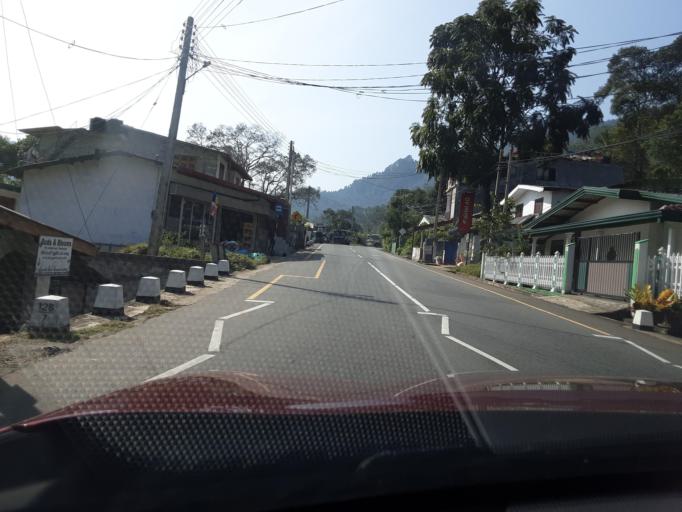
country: LK
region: Uva
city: Badulla
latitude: 6.9675
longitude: 81.0892
